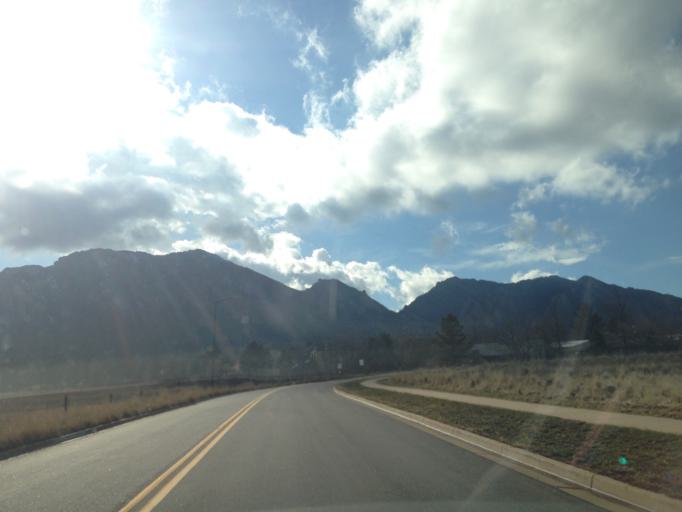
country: US
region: Colorado
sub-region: Boulder County
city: Boulder
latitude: 39.9644
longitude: -105.2515
